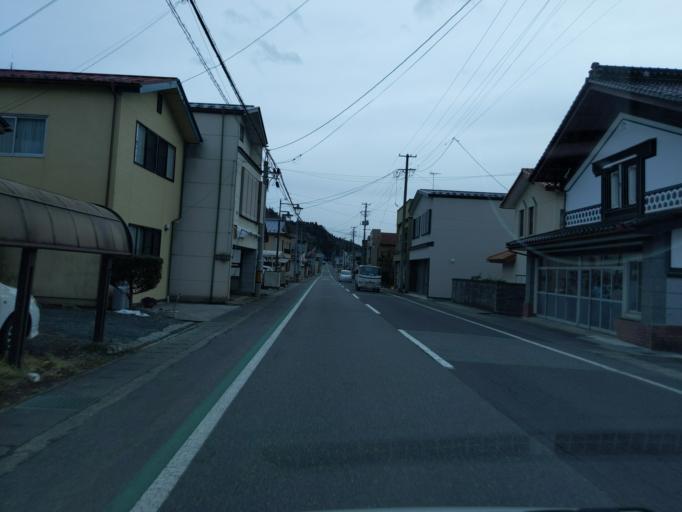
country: JP
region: Iwate
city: Mizusawa
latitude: 39.0377
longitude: 141.2945
